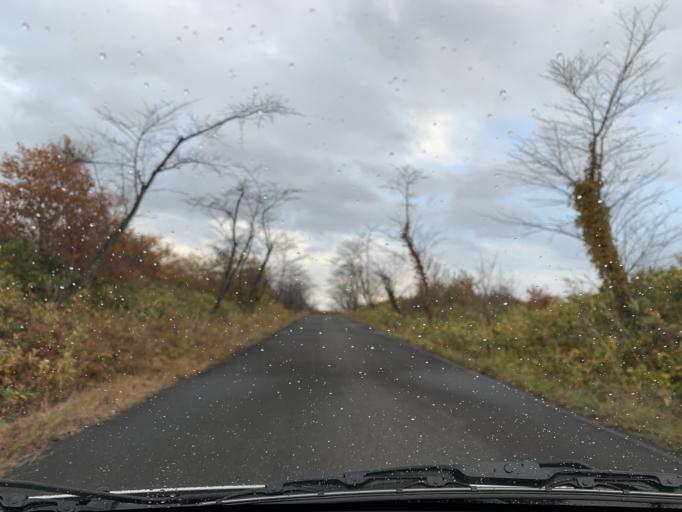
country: JP
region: Iwate
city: Mizusawa
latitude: 39.0883
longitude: 141.0083
